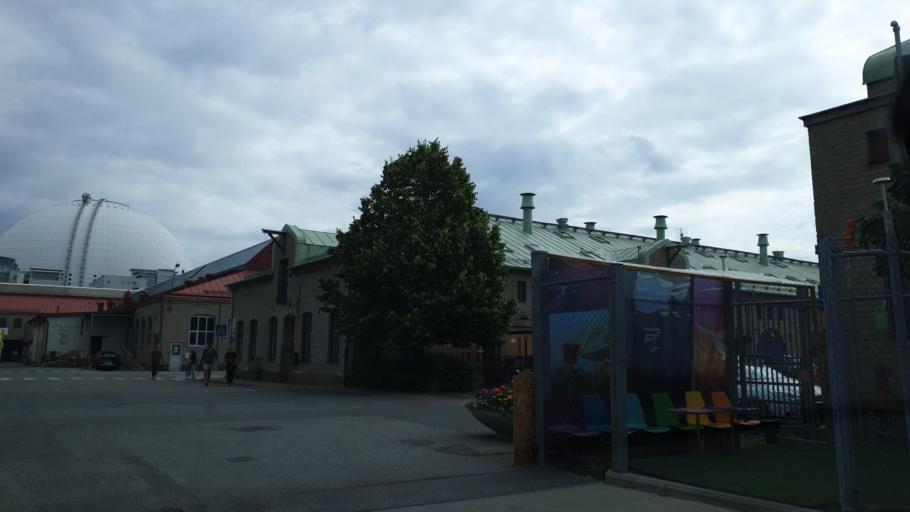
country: SE
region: Stockholm
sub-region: Stockholms Kommun
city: Arsta
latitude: 59.2917
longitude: 18.0763
